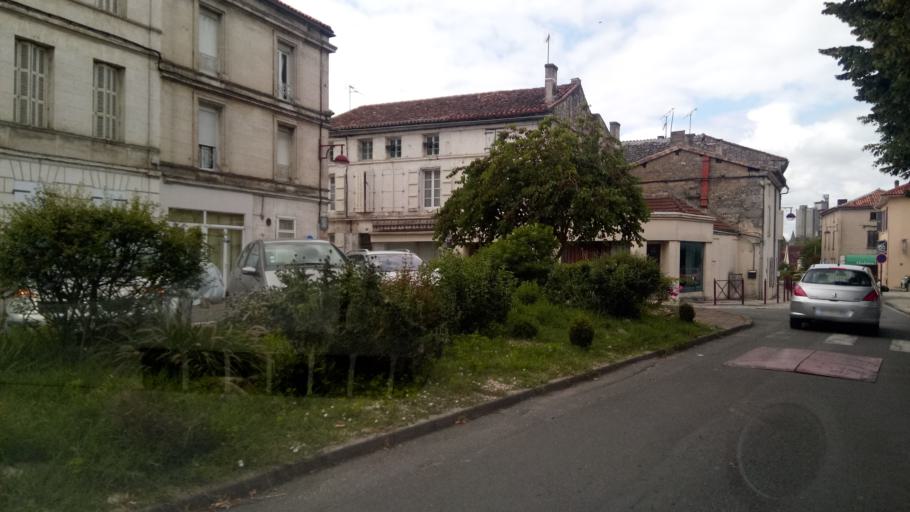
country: FR
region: Poitou-Charentes
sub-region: Departement de la Charente
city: La Couronne
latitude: 45.6086
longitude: 0.1011
